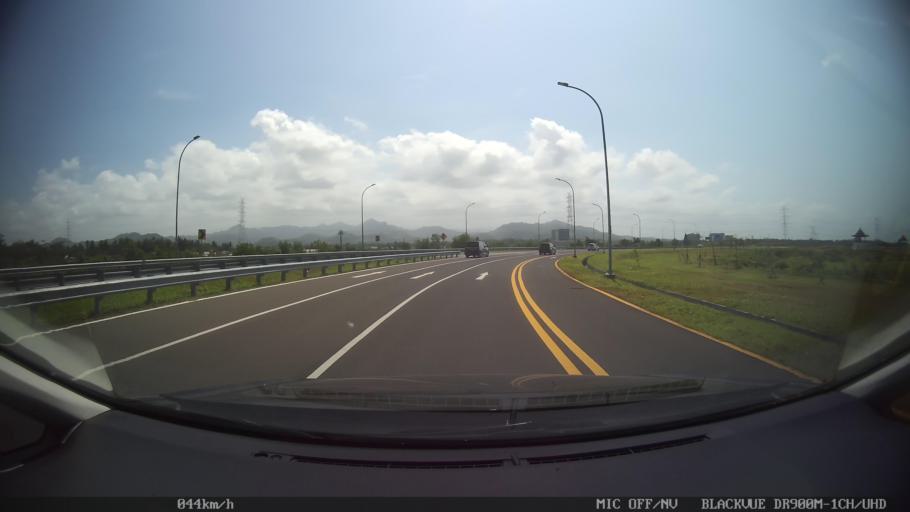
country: ID
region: Daerah Istimewa Yogyakarta
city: Srandakan
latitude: -7.8928
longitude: 110.0583
